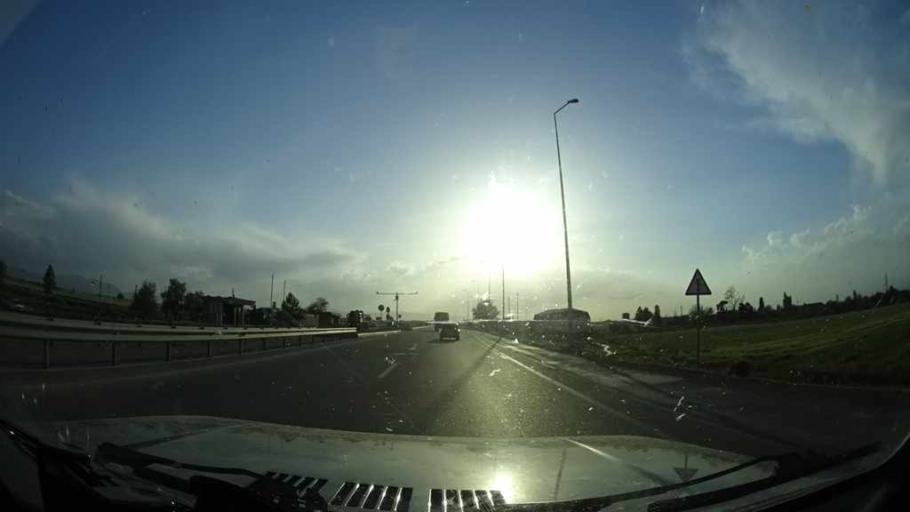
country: AZ
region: Samux
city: Samux
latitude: 40.6898
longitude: 46.5134
